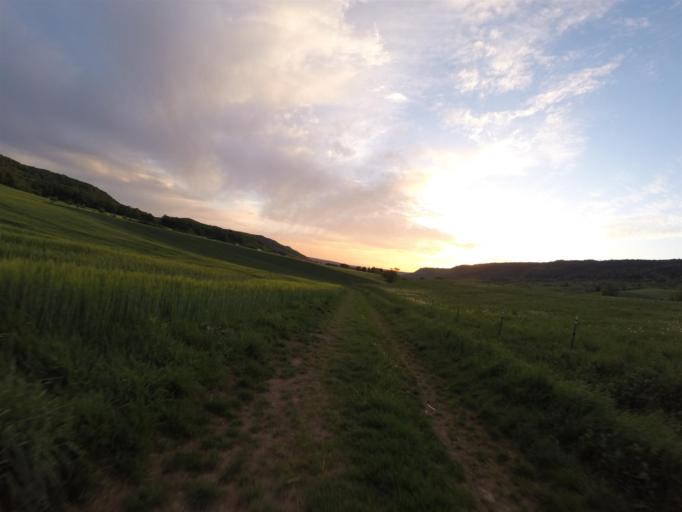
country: DE
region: Thuringia
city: Grosslobichau
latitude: 50.9301
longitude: 11.6680
